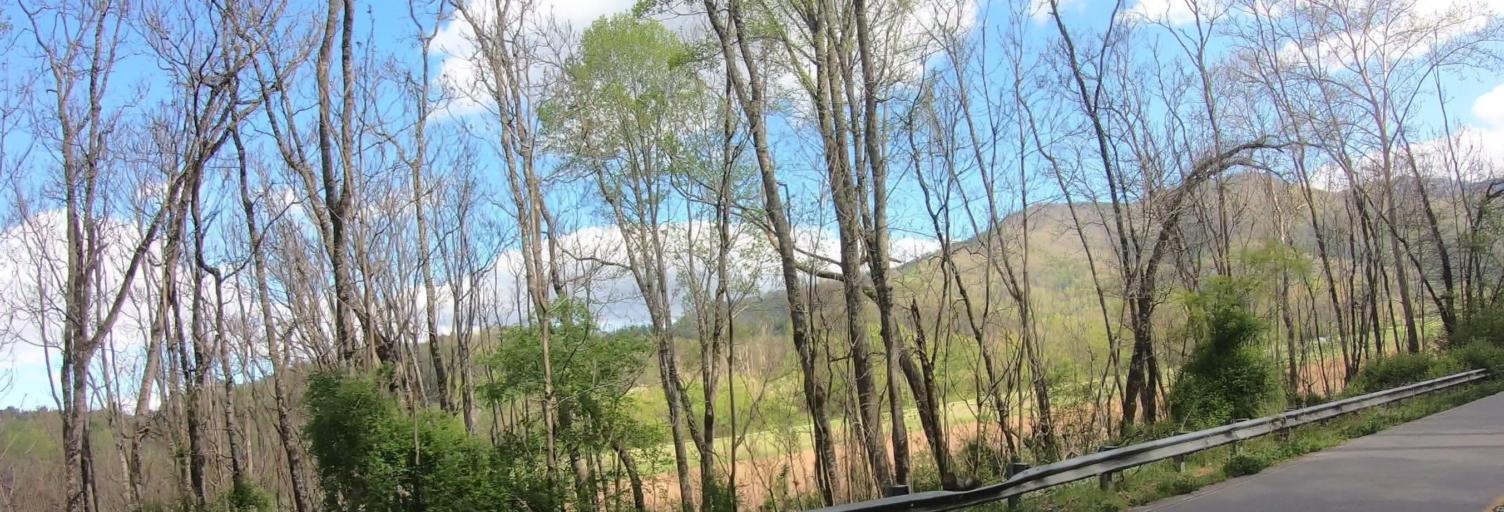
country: US
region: North Carolina
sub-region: Swain County
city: Bryson City
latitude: 35.4431
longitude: -83.3995
